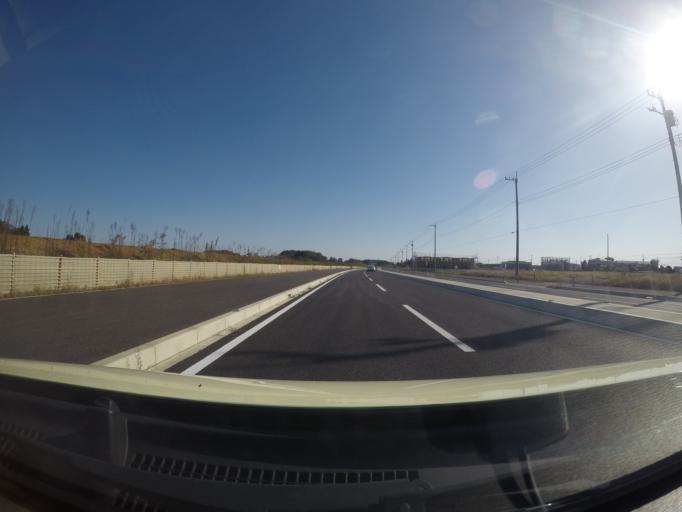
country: JP
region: Ibaraki
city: Naka
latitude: 36.1039
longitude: 140.1243
